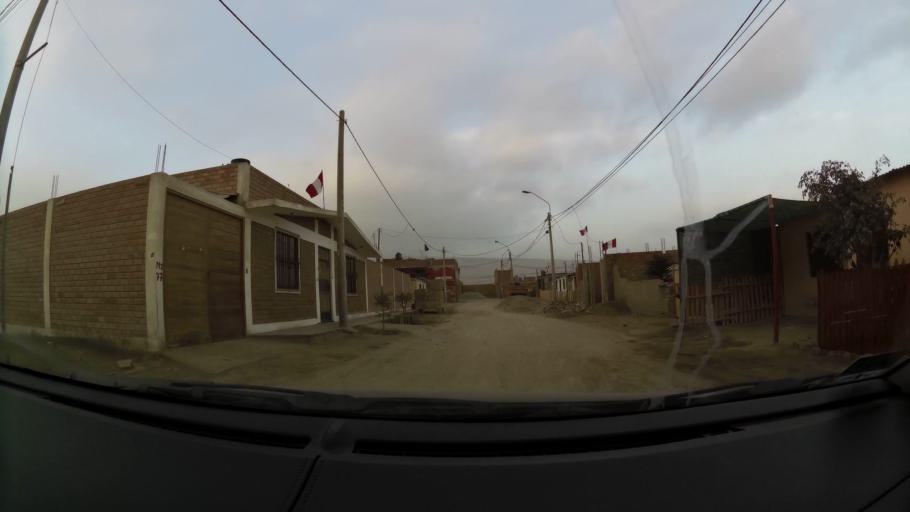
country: PE
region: Lima
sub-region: Lima
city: Santa Rosa
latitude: -11.7324
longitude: -77.1432
